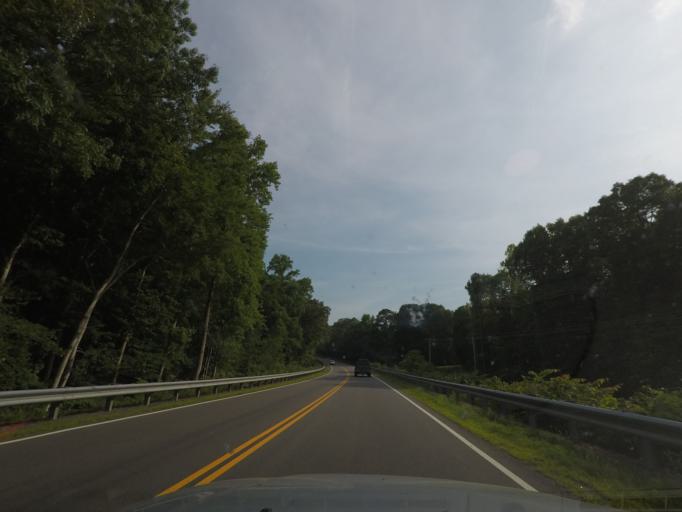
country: US
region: Virginia
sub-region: Mecklenburg County
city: Chase City
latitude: 36.8180
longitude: -78.5980
